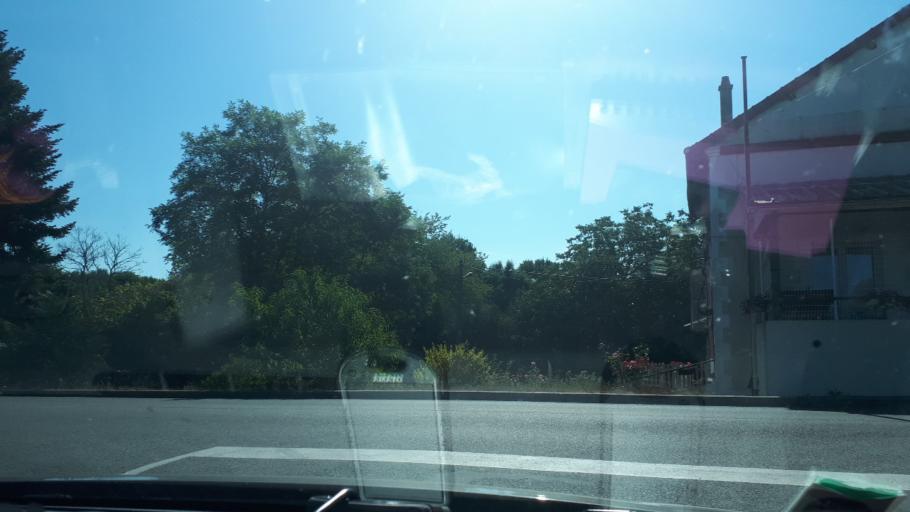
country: FR
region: Centre
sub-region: Departement du Loiret
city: Briare
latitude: 47.5996
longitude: 2.7627
